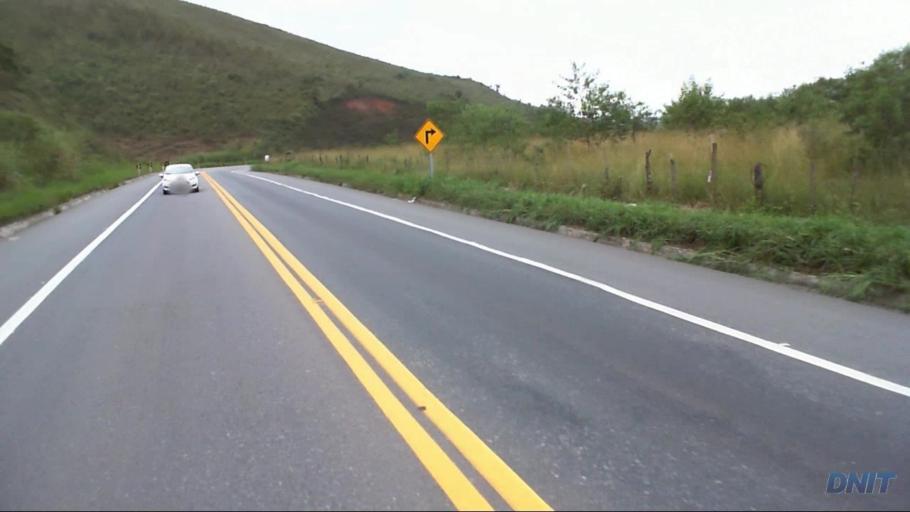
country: BR
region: Minas Gerais
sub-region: Nova Era
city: Nova Era
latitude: -19.6849
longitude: -42.9875
